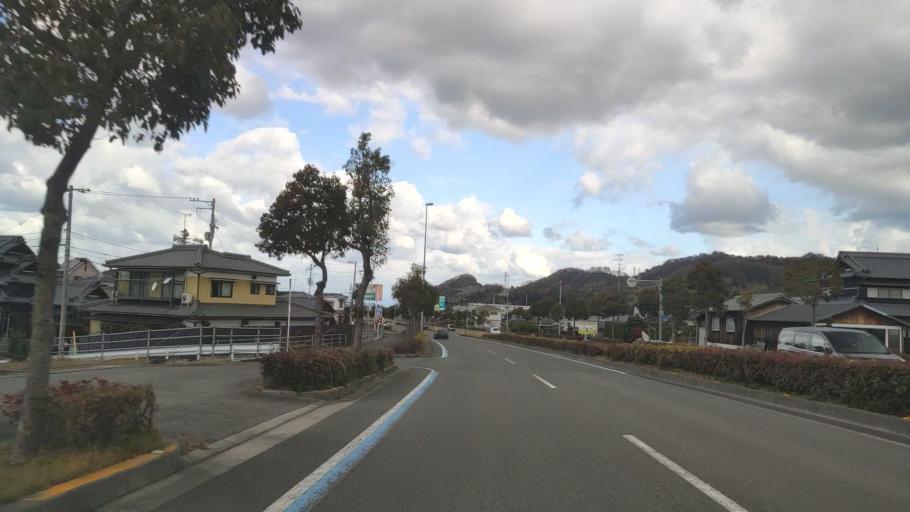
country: JP
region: Ehime
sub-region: Shikoku-chuo Shi
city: Matsuyama
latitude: 33.8964
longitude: 132.7582
